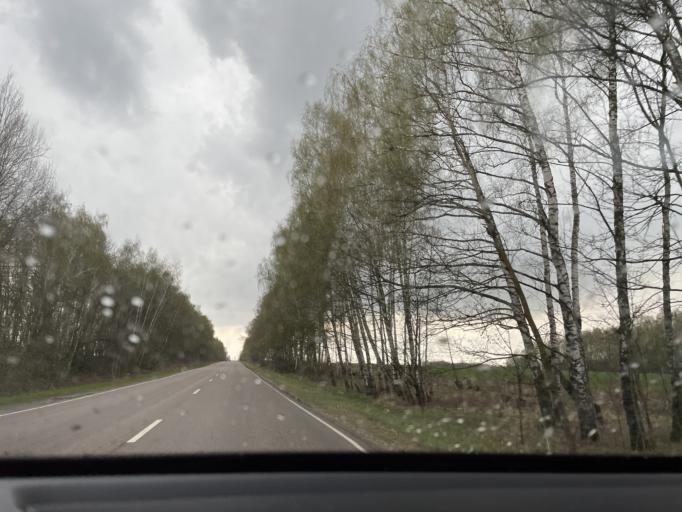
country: RU
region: Tula
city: Novogurovskiy
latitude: 54.5292
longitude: 37.3317
